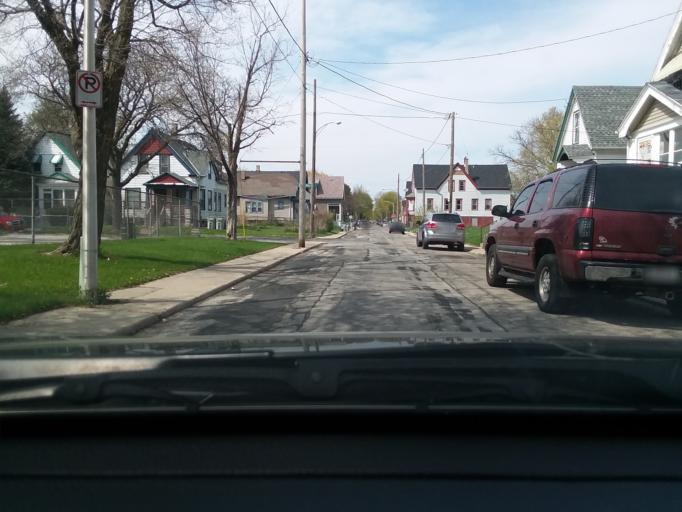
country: US
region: Wisconsin
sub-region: Milwaukee County
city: Milwaukee
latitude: 43.0737
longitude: -87.9276
